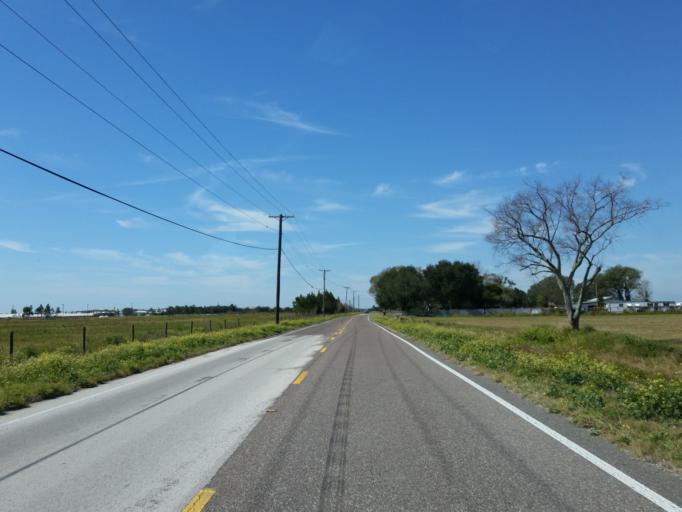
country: US
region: Florida
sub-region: Hillsborough County
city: Balm
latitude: 27.7626
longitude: -82.2181
